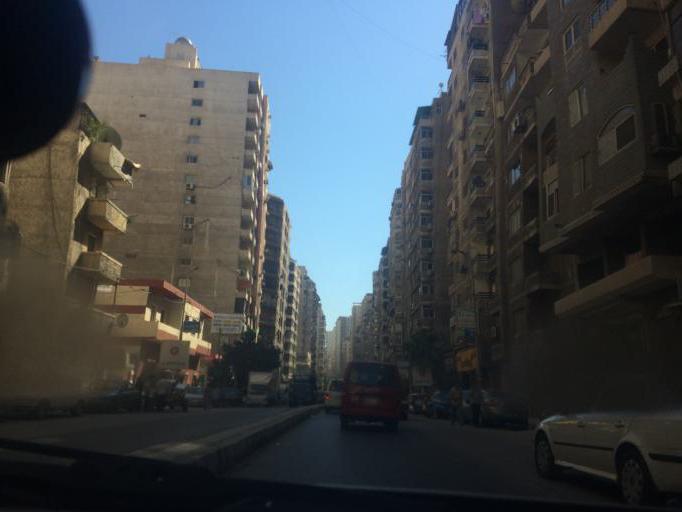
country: EG
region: Alexandria
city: Alexandria
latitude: 31.2792
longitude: 30.0113
